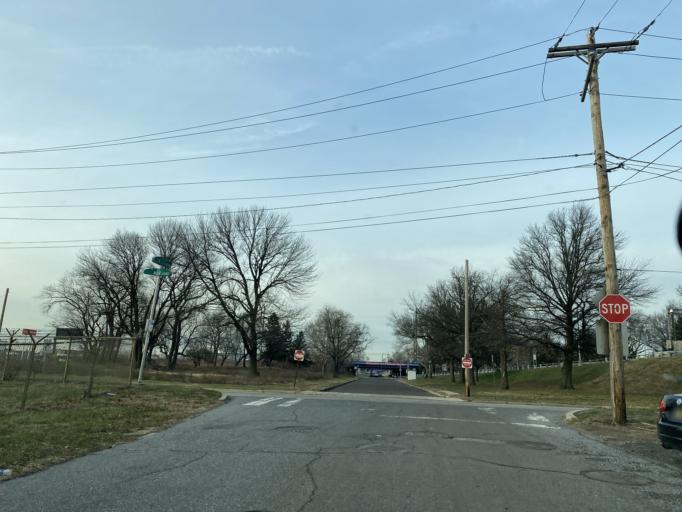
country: US
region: New Jersey
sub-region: Burlington County
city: Palmyra
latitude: 40.0159
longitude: -75.0468
